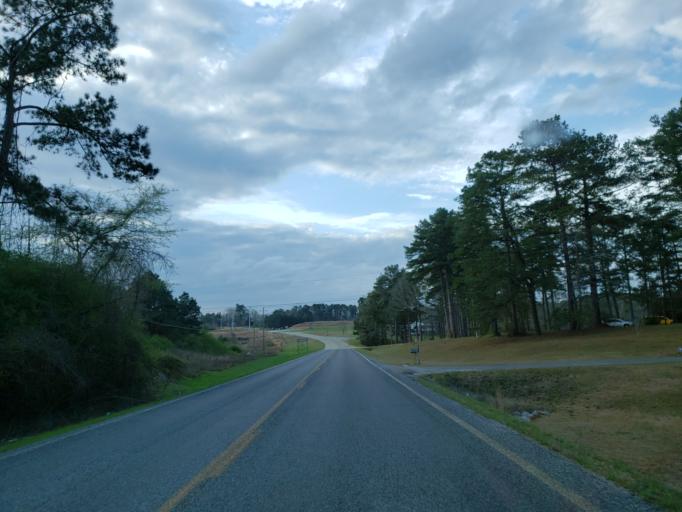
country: US
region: Mississippi
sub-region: Clarke County
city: Stonewall
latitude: 32.2097
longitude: -88.6942
